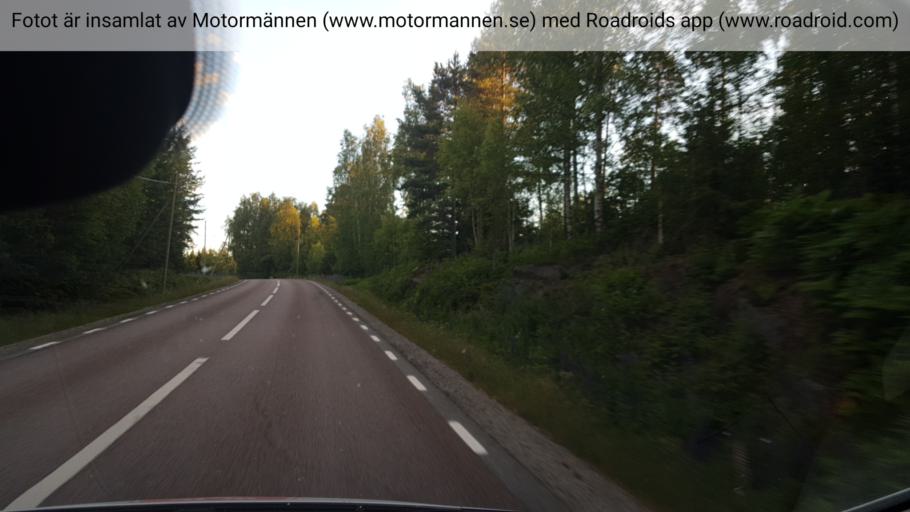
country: SE
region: Vaermland
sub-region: Sunne Kommun
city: Sunne
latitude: 59.6636
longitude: 12.9631
